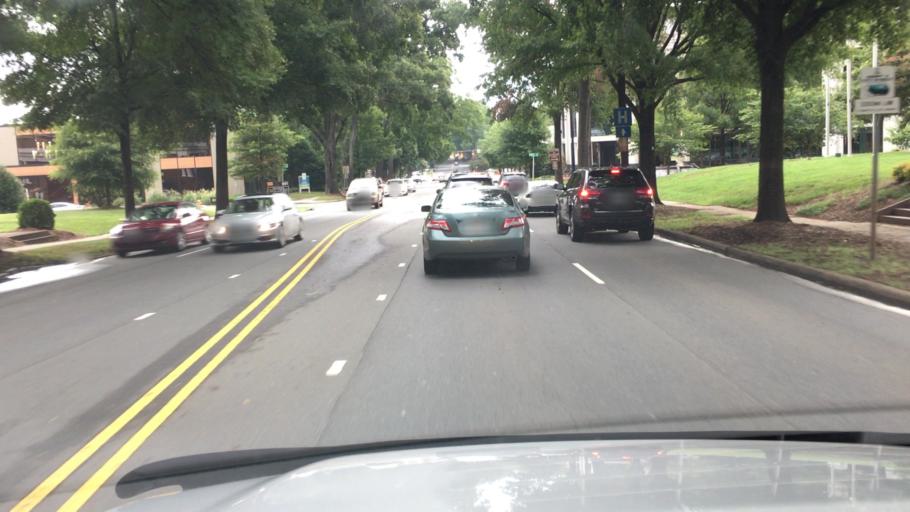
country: US
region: North Carolina
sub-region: Mecklenburg County
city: Charlotte
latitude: 35.2155
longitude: -80.8462
